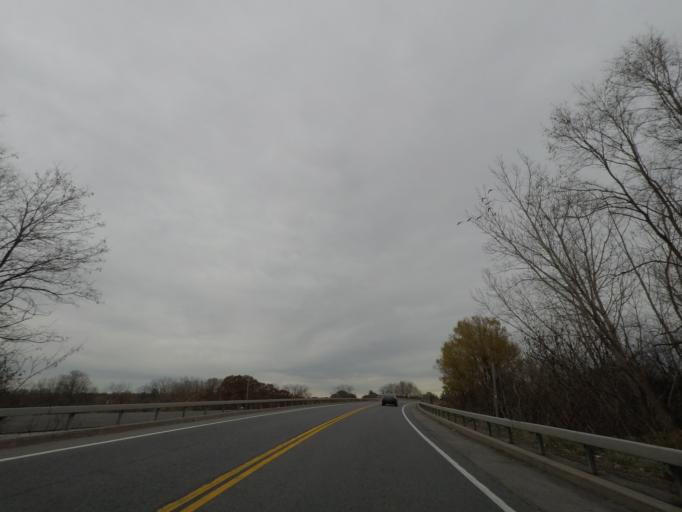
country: US
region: New York
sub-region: Saratoga County
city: Country Knolls
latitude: 42.8931
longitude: -73.8263
